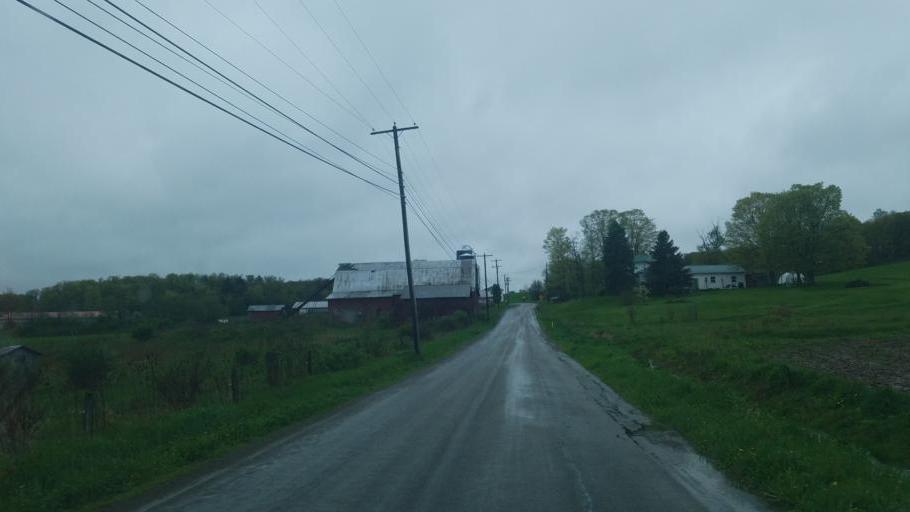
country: US
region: Pennsylvania
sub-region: Potter County
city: Galeton
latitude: 41.9068
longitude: -77.7740
